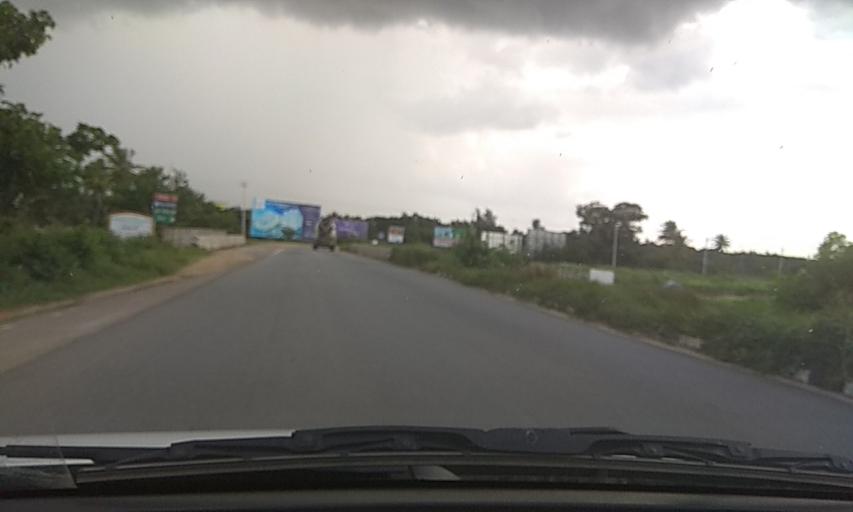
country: IN
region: Karnataka
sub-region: Mandya
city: Shrirangapattana
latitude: 12.3877
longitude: 76.6671
